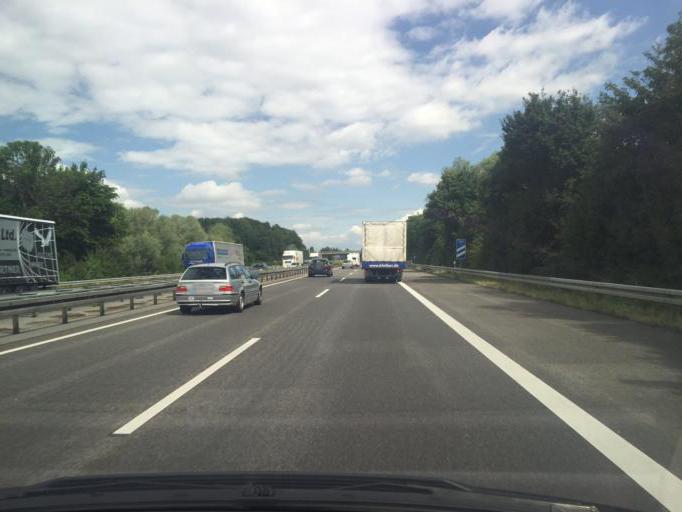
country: DE
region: Hesse
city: Zwingenberg
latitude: 49.7197
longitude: 8.5947
